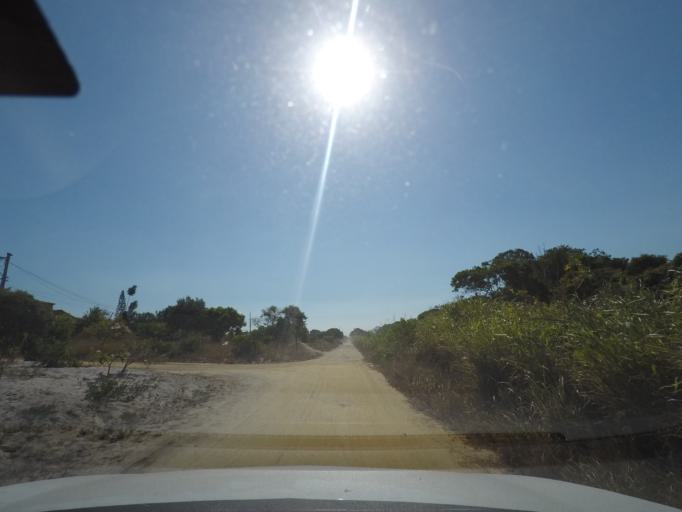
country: BR
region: Rio de Janeiro
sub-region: Marica
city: Marica
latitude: -22.9652
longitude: -42.9135
